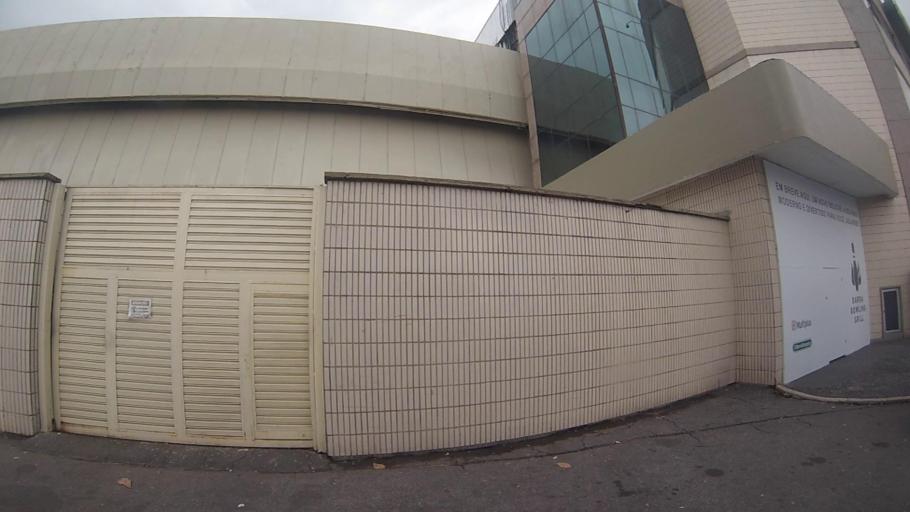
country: BR
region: Rio de Janeiro
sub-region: Rio De Janeiro
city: Rio de Janeiro
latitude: -22.9970
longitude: -43.3586
